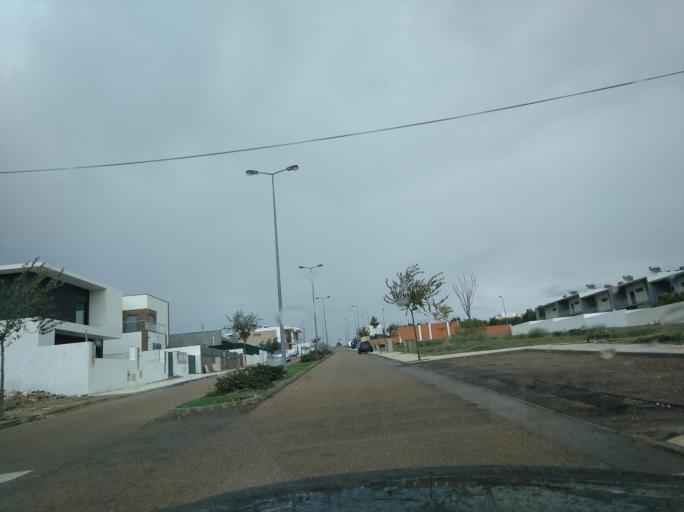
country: PT
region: Portalegre
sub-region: Elvas
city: Elvas
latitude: 38.8656
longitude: -7.1621
